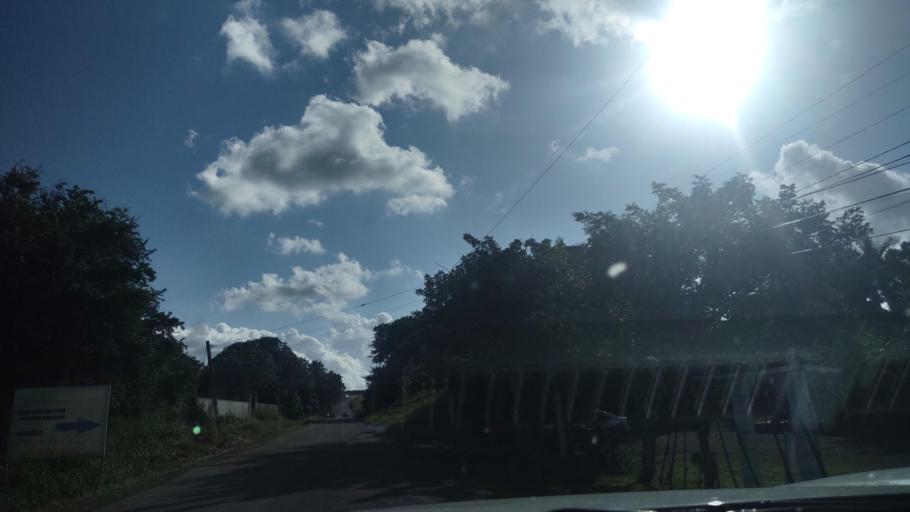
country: MX
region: Veracruz
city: El Tejar
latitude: 19.0671
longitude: -96.1745
